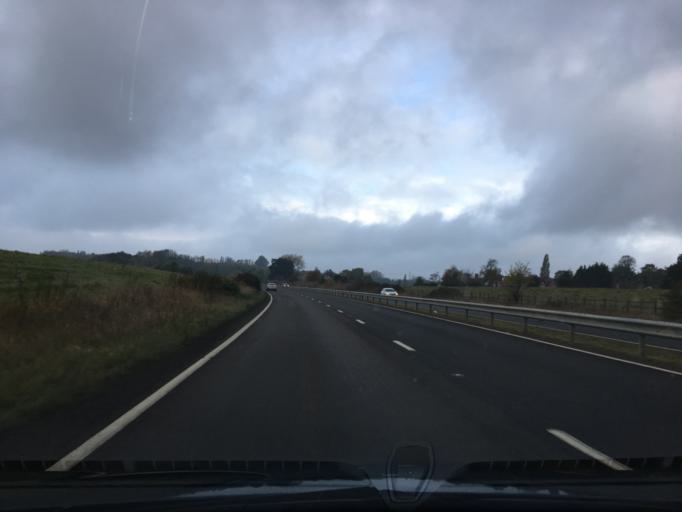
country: GB
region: England
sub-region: Hampshire
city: Kingsley
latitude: 51.1866
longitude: -0.8842
